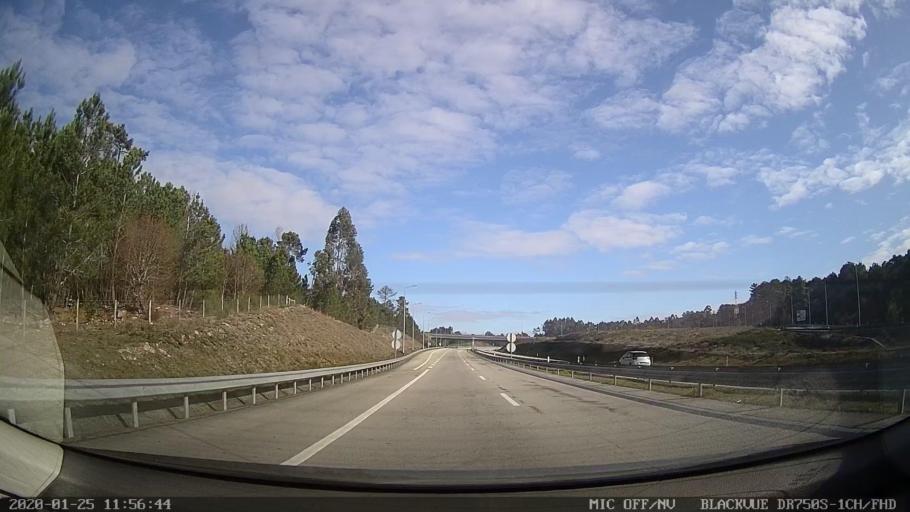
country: PT
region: Viseu
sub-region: Viseu
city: Campo
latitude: 40.7060
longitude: -7.9479
